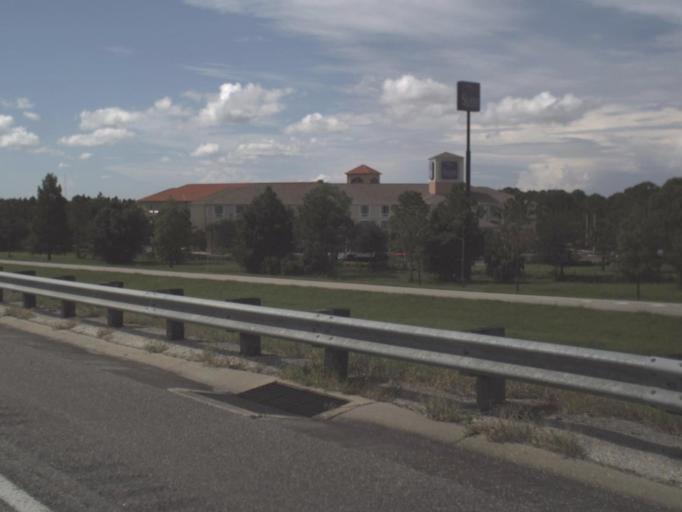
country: US
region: Florida
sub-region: Charlotte County
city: Harbour Heights
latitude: 27.0194
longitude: -82.0481
